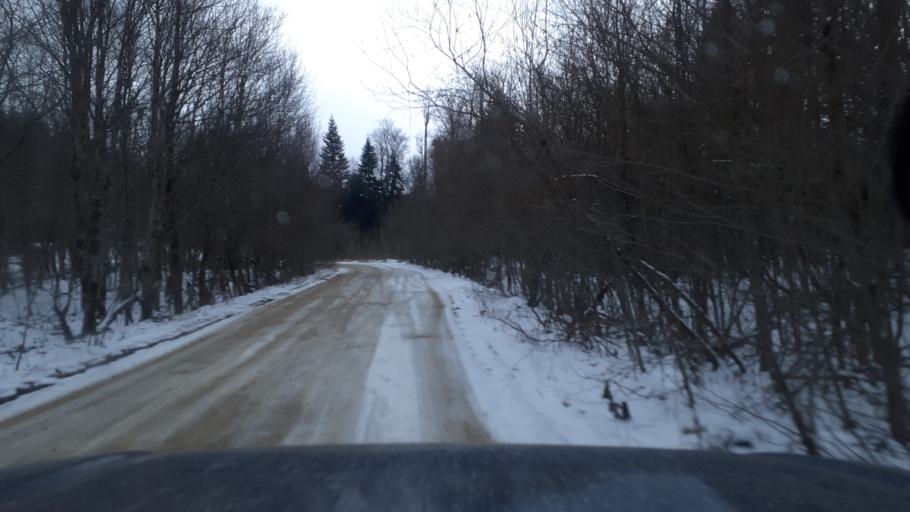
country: RU
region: Krasnodarskiy
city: Neftegorsk
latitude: 44.0766
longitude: 39.8045
